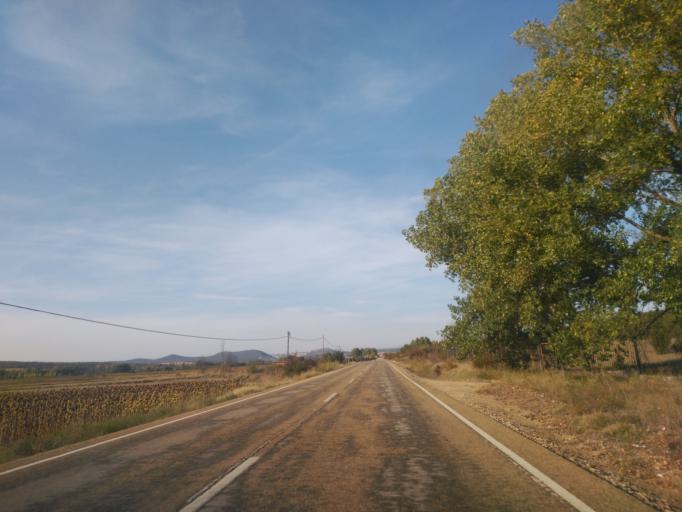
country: ES
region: Castille and Leon
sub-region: Provincia de Soria
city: Valdemaluque
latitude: 41.6581
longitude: -3.0510
